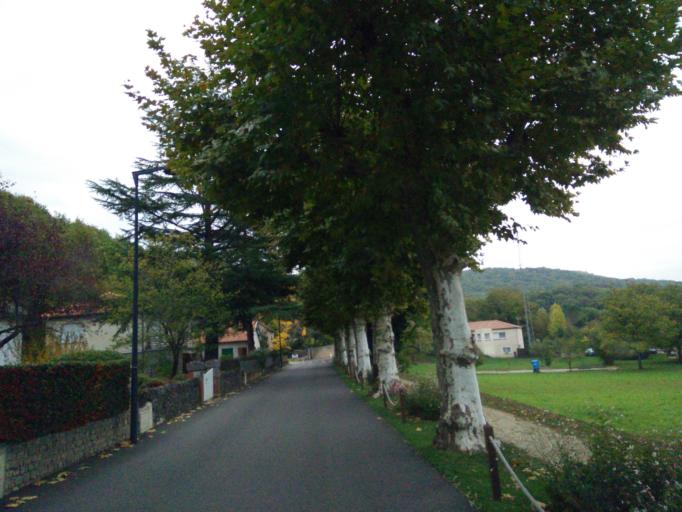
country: FR
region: Midi-Pyrenees
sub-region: Departement du Lot
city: Lalbenque
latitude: 44.4785
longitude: 1.5824
